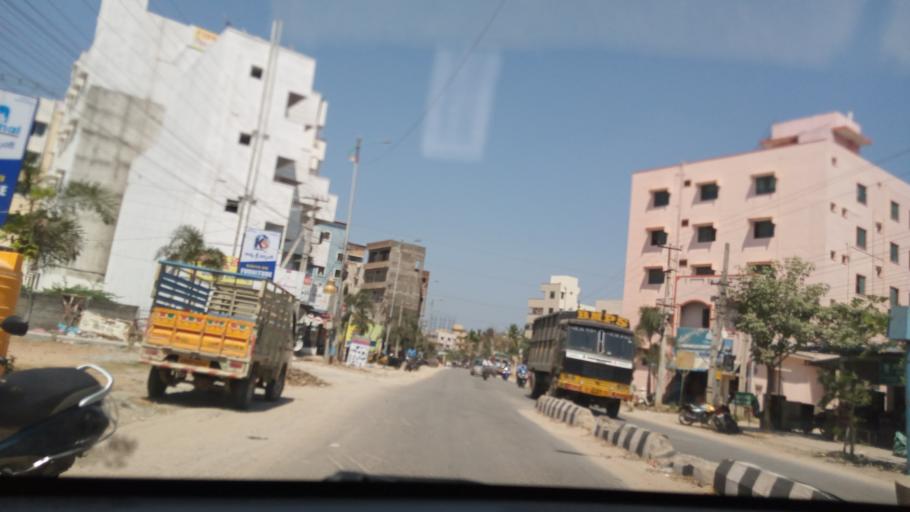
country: IN
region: Andhra Pradesh
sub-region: Chittoor
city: Tirupati
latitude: 13.6123
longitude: 79.4146
